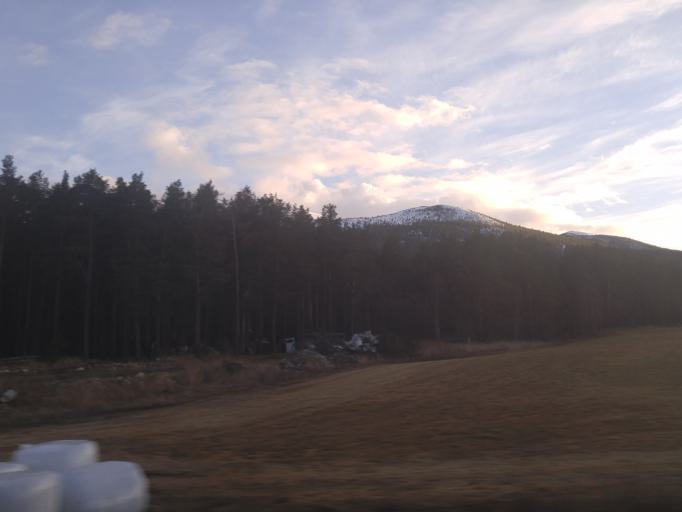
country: NO
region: Oppland
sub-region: Dovre
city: Dovre
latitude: 61.9526
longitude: 9.2738
